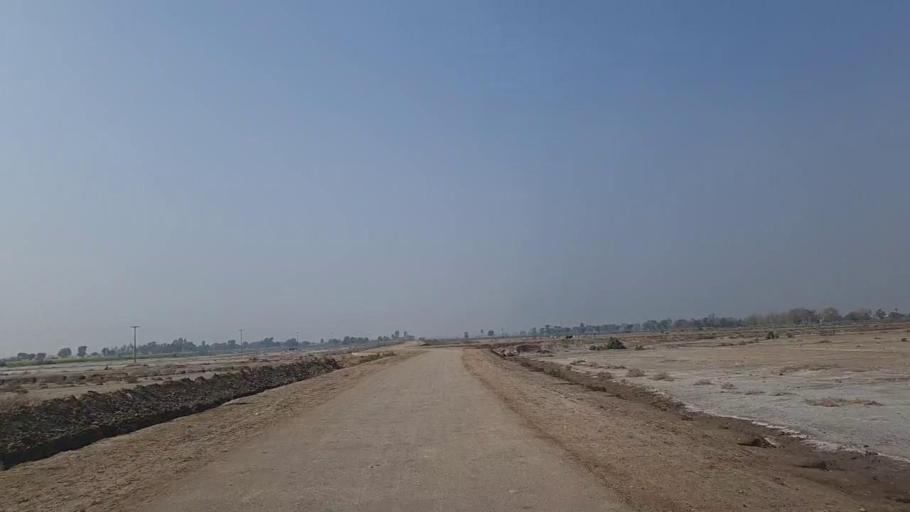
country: PK
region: Sindh
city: Nawabshah
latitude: 26.3601
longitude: 68.4312
